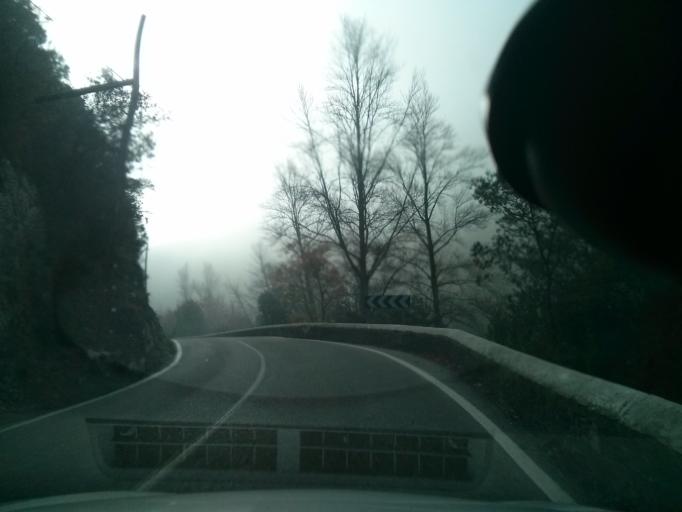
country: ES
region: Castille and Leon
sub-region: Provincia de Burgos
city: Medina de Pomar
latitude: 42.8721
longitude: -3.5960
